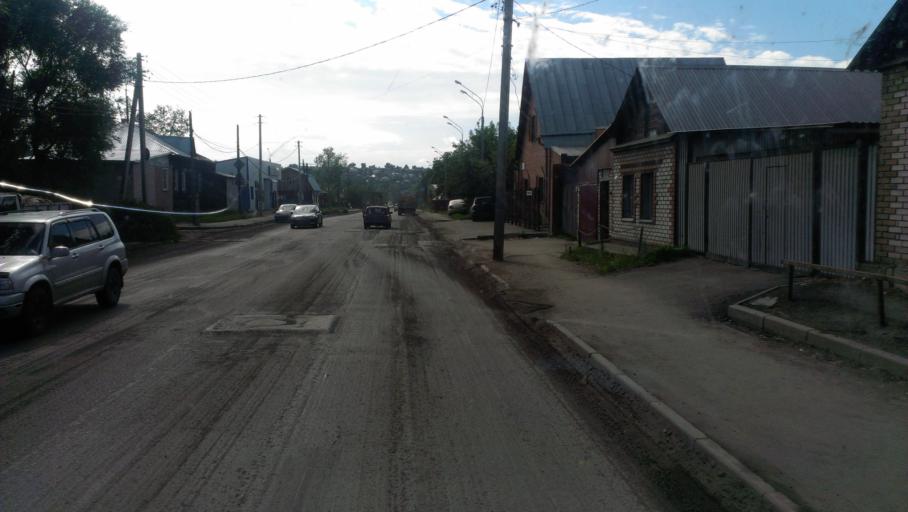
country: RU
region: Altai Krai
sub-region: Gorod Barnaulskiy
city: Barnaul
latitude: 53.3269
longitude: 83.7636
